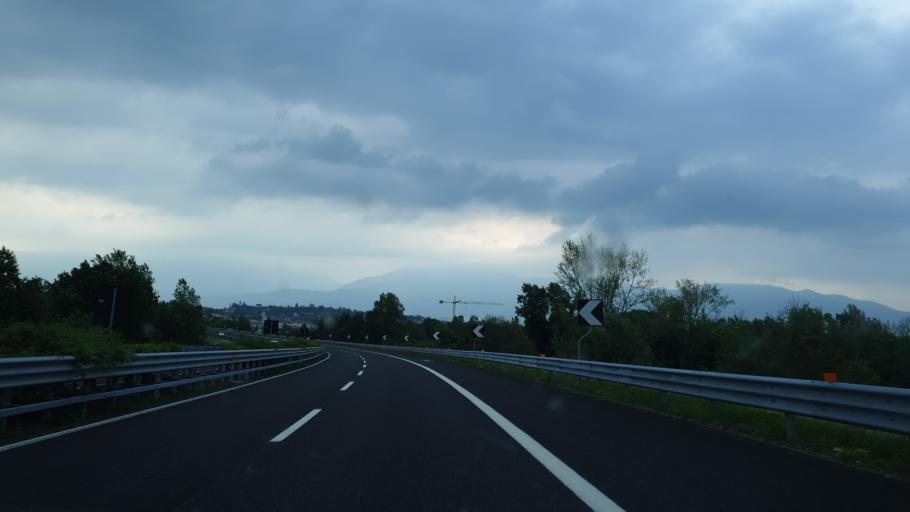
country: IT
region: Veneto
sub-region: Provincia di Treviso
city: San Martino
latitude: 45.9029
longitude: 12.3452
